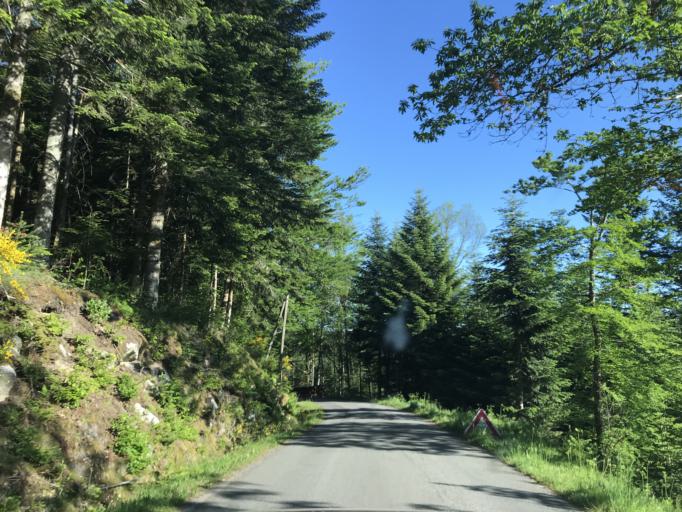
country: FR
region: Auvergne
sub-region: Departement du Puy-de-Dome
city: Job
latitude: 45.7052
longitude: 3.7081
